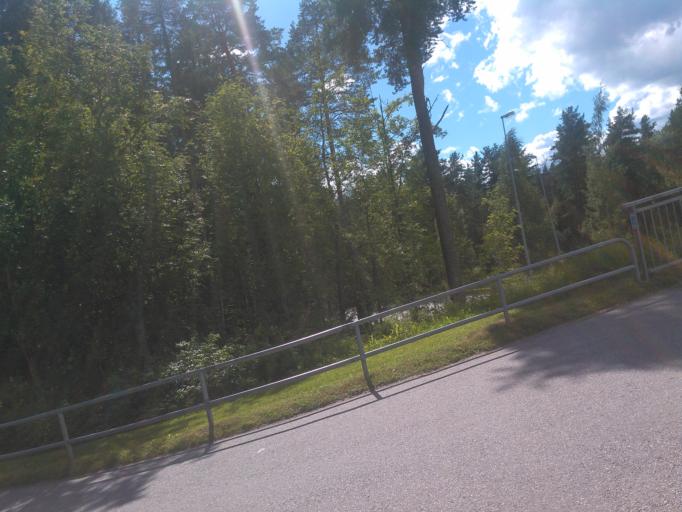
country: SE
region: Vaesterbotten
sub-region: Umea Kommun
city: Umea
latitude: 63.8134
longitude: 20.3062
